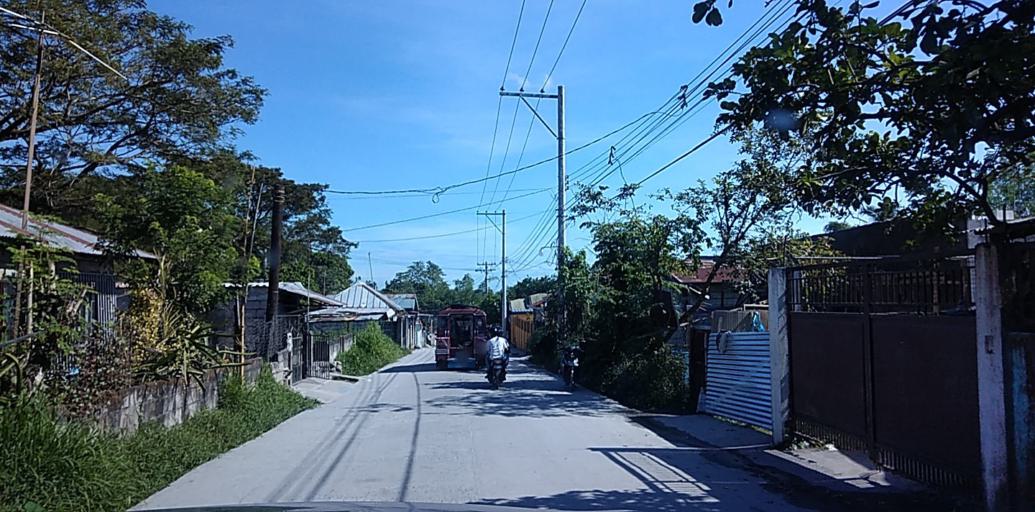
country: PH
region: Central Luzon
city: Santol
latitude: 15.1680
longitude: 120.5073
